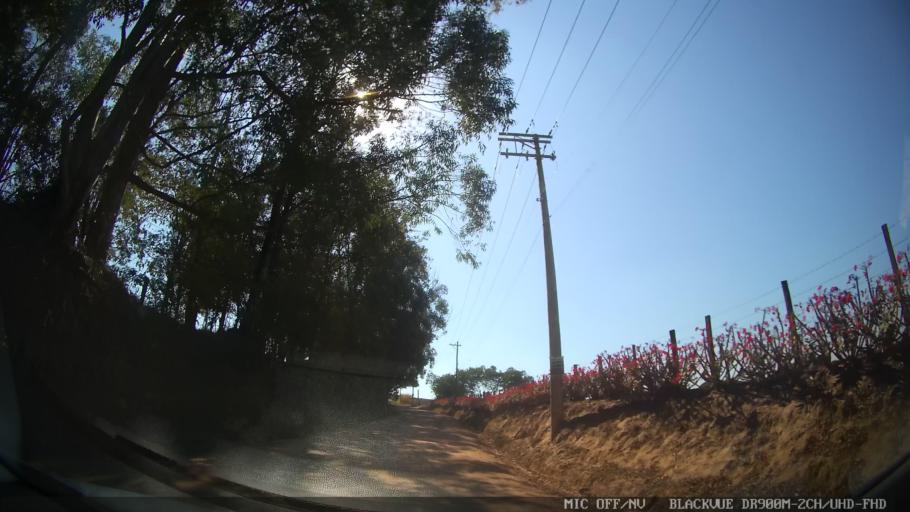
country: BR
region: Sao Paulo
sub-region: Itupeva
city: Itupeva
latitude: -23.1165
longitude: -47.0865
